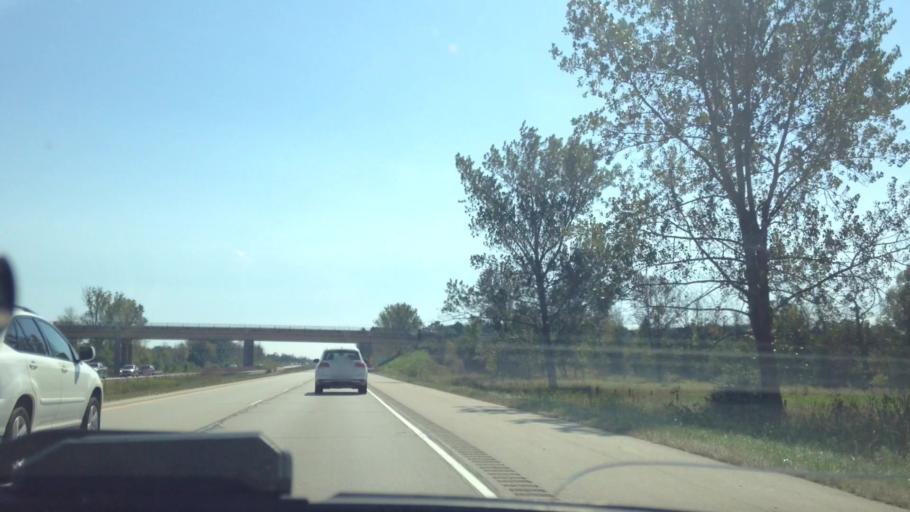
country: US
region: Wisconsin
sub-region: Ozaukee County
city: Thiensville
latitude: 43.2522
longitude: -87.9201
